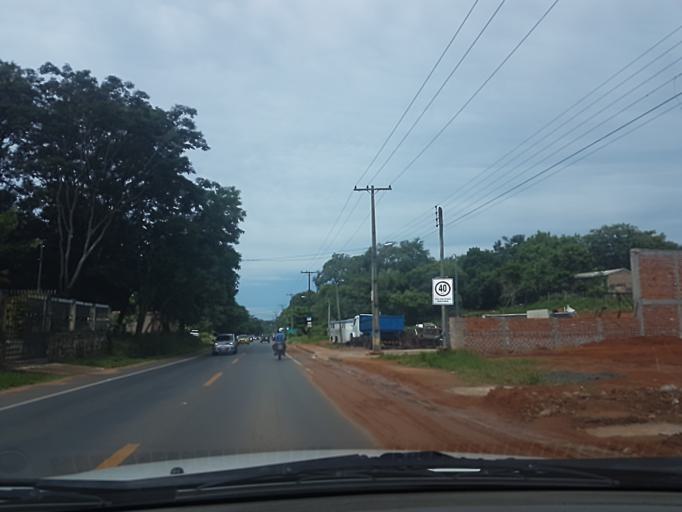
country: PY
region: Central
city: Limpio
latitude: -25.2384
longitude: -57.4544
